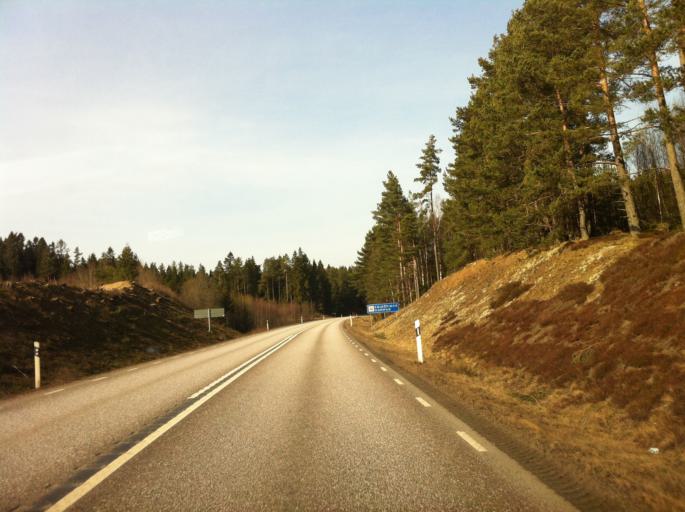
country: SE
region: Vaestra Goetaland
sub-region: Skovde Kommun
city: Skultorp
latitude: 58.2426
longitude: 13.8200
